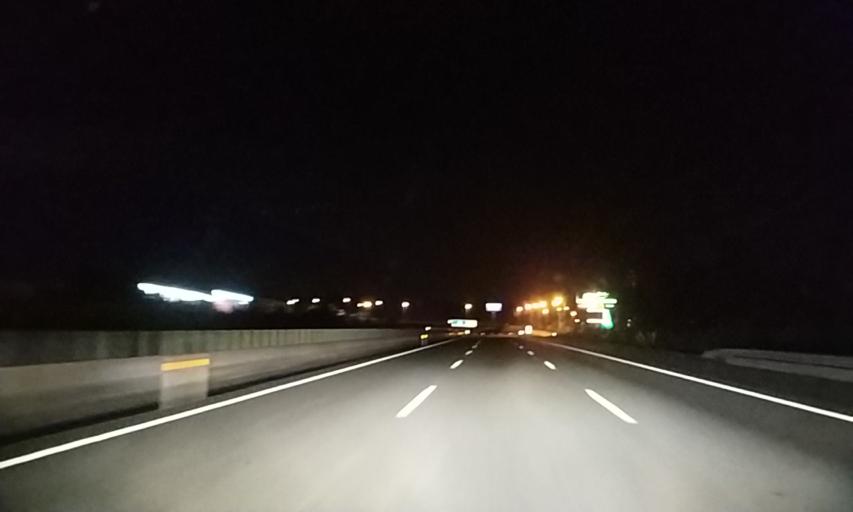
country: PT
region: Aveiro
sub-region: Santa Maria da Feira
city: Feira
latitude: 40.9194
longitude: -8.5675
